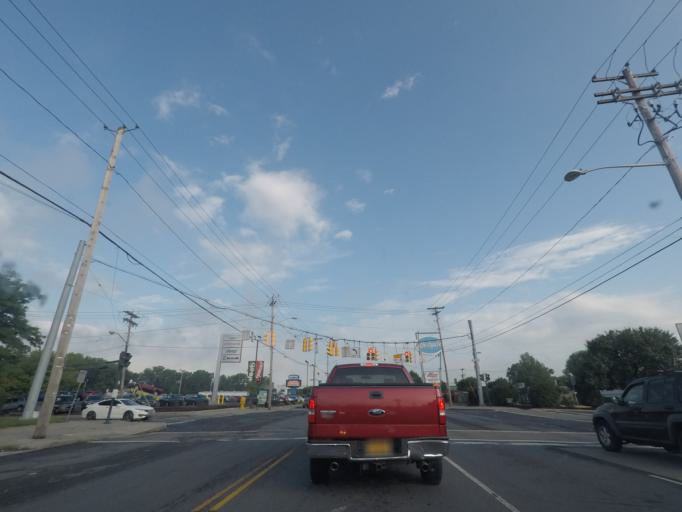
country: US
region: New York
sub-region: Albany County
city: West Albany
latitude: 42.6813
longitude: -73.7914
